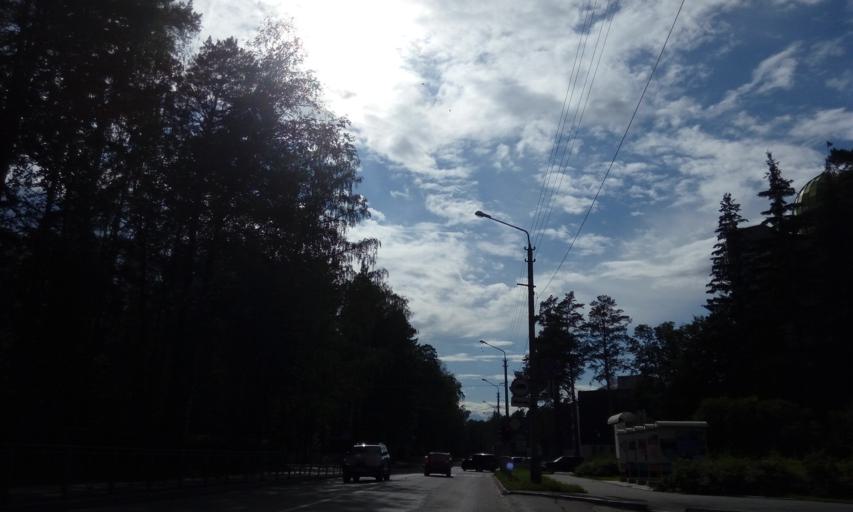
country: RU
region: Novosibirsk
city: Akademgorodok
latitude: 54.8427
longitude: 83.0937
